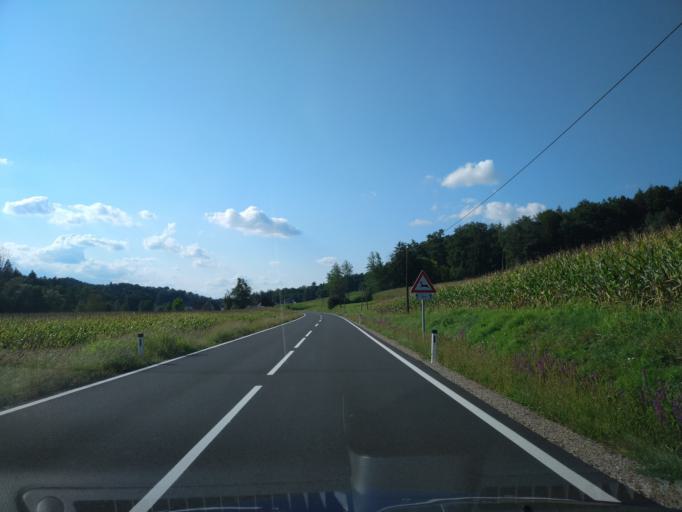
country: AT
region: Styria
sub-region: Politischer Bezirk Leibnitz
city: Sankt Johann im Saggautal
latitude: 46.7245
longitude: 15.4017
